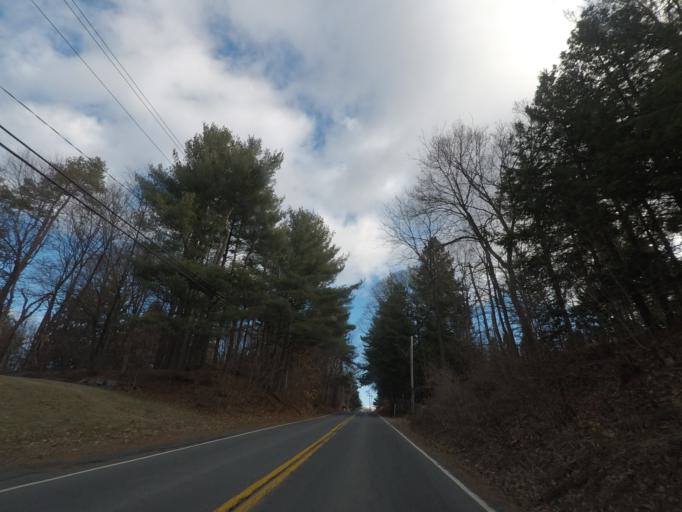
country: US
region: New York
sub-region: Saratoga County
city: Waterford
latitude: 42.7910
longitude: -73.6533
